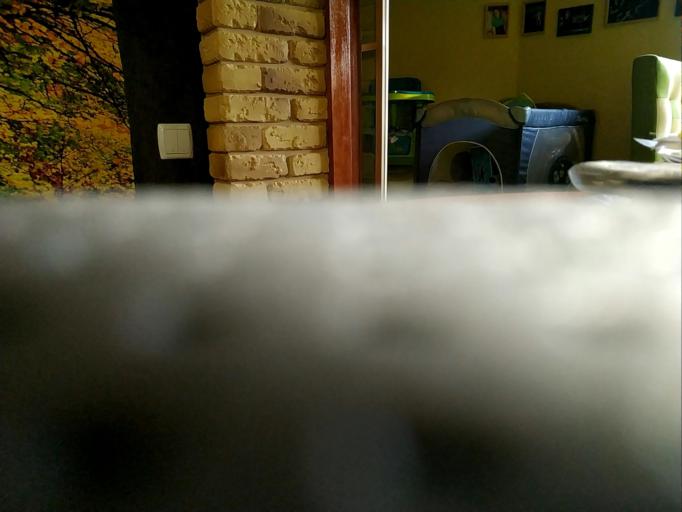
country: RU
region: Kaluga
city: Seredeyskiy
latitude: 53.8584
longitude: 35.3713
